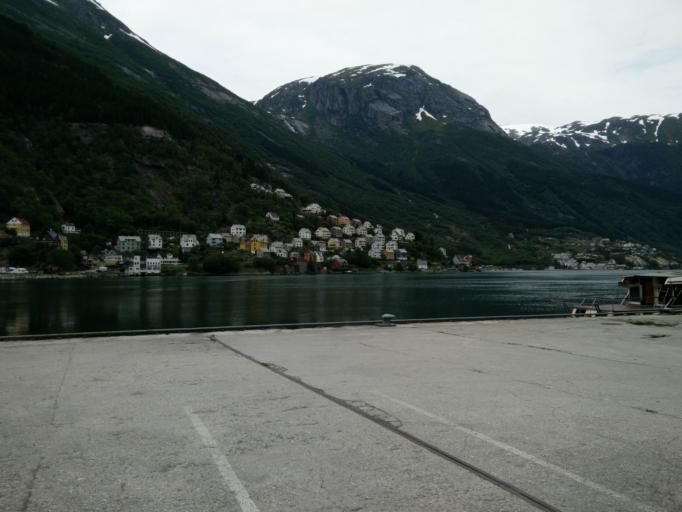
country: NO
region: Hordaland
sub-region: Odda
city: Odda
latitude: 60.0707
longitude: 6.5468
